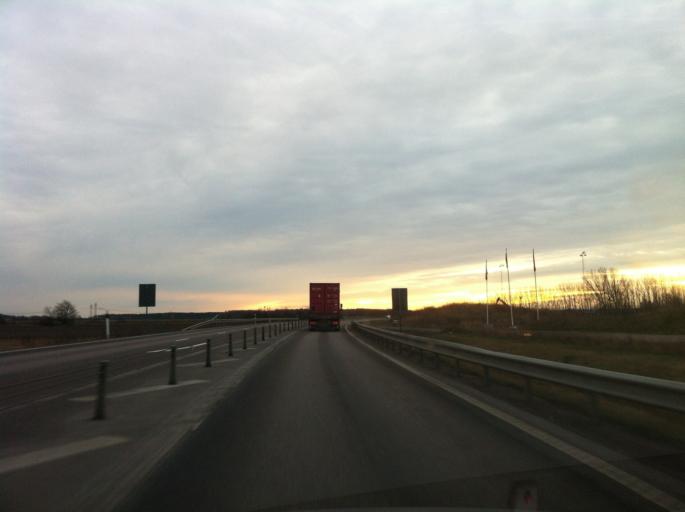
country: SE
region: Skane
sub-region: Hoganas Kommun
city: Hoganas
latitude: 56.1448
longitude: 12.5962
